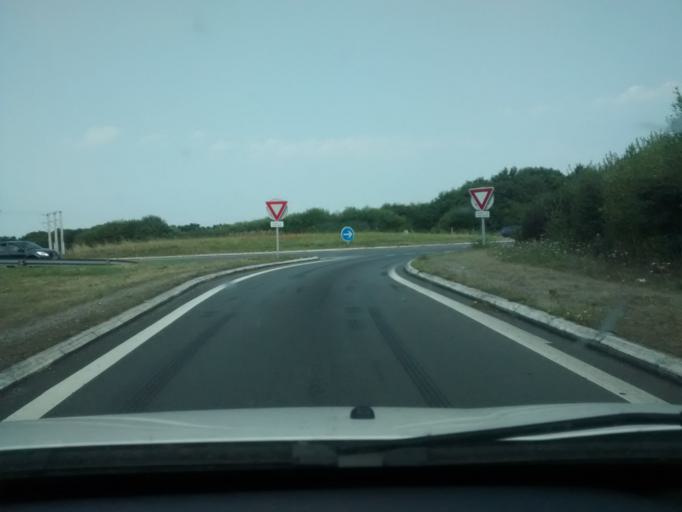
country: FR
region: Pays de la Loire
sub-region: Departement de la Loire-Atlantique
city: Saint-Andre-des-Eaux
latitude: 47.2849
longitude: -2.3003
